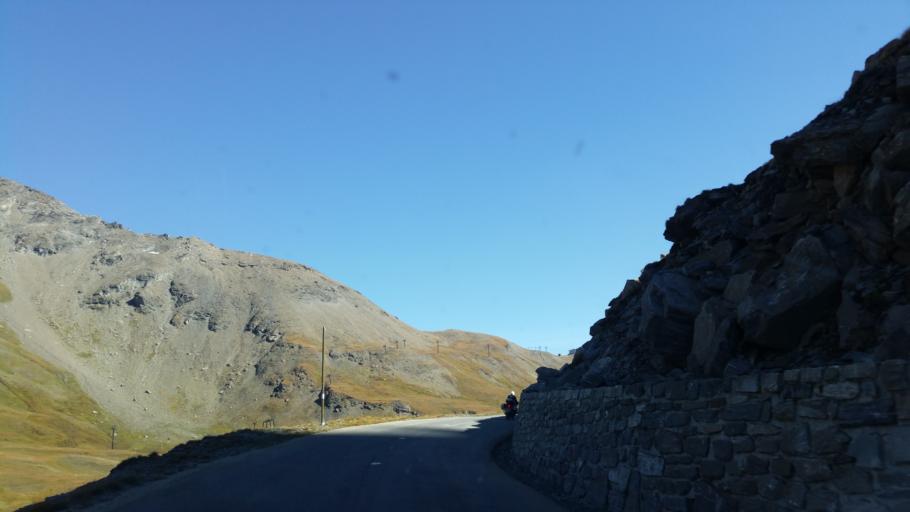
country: FR
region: Rhone-Alpes
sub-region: Departement de la Savoie
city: Val-d'Isere
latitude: 45.4333
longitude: 7.0162
